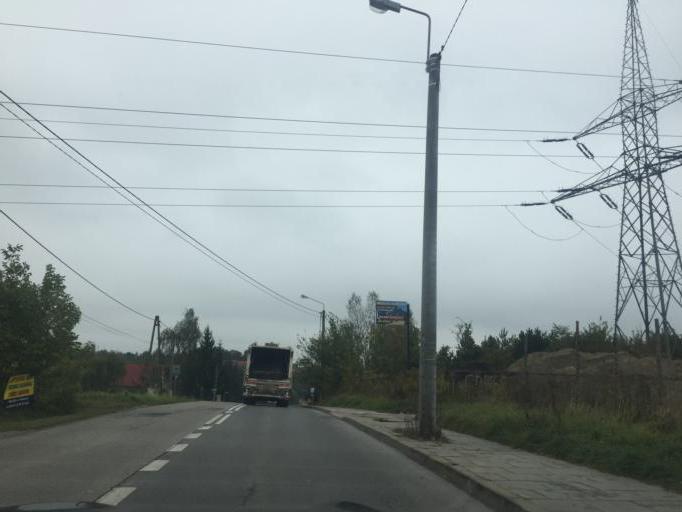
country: PL
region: Lesser Poland Voivodeship
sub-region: Powiat wielicki
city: Wieliczka
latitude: 49.9942
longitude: 20.0203
